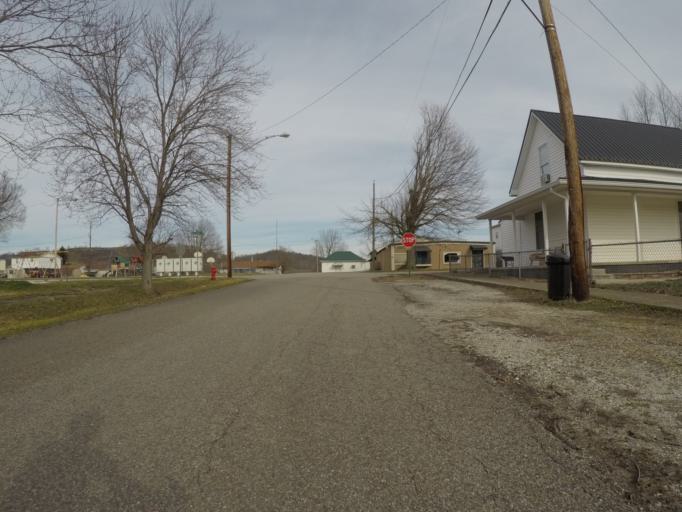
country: US
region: West Virginia
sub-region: Cabell County
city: Pea Ridge
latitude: 38.4387
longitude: -82.3794
